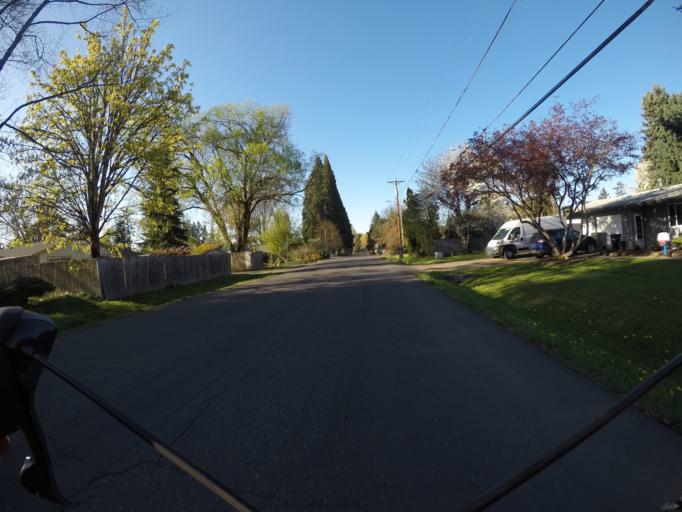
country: US
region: Oregon
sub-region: Washington County
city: Aloha
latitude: 45.4816
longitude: -122.8751
